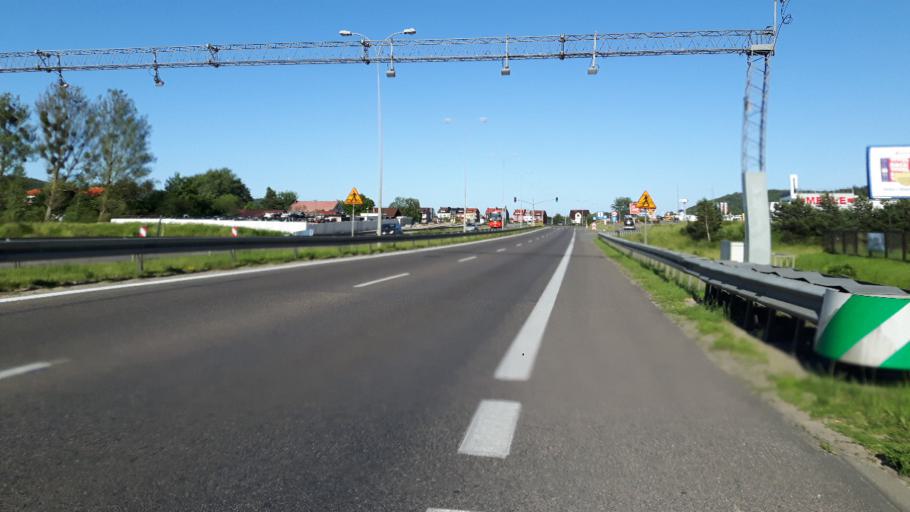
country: PL
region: Pomeranian Voivodeship
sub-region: Powiat wejherowski
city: Wejherowo
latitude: 54.6029
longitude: 18.2878
